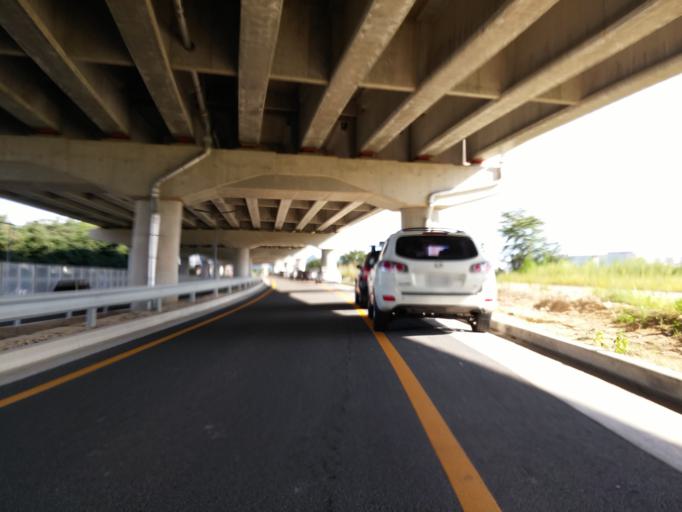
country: KR
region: Daejeon
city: Songgang-dong
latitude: 36.4415
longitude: 127.3914
